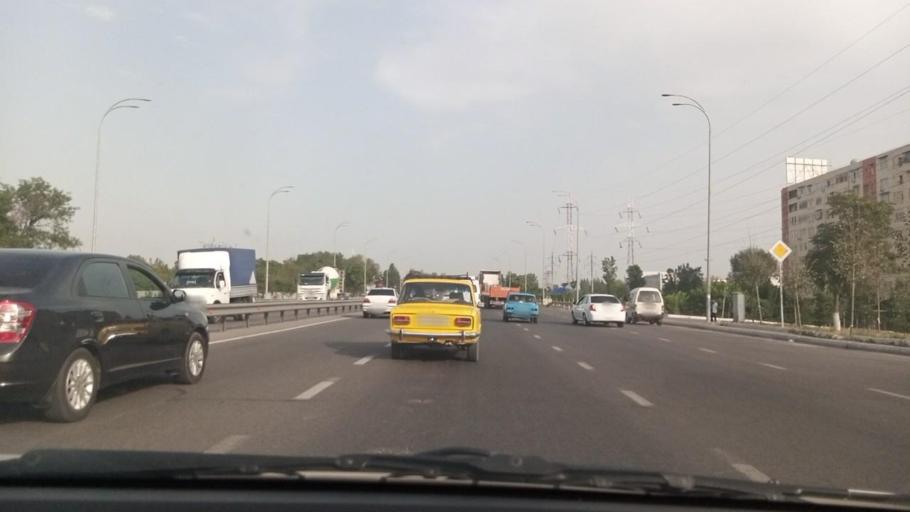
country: UZ
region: Toshkent Shahri
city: Bektemir
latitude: 41.2573
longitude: 69.3800
